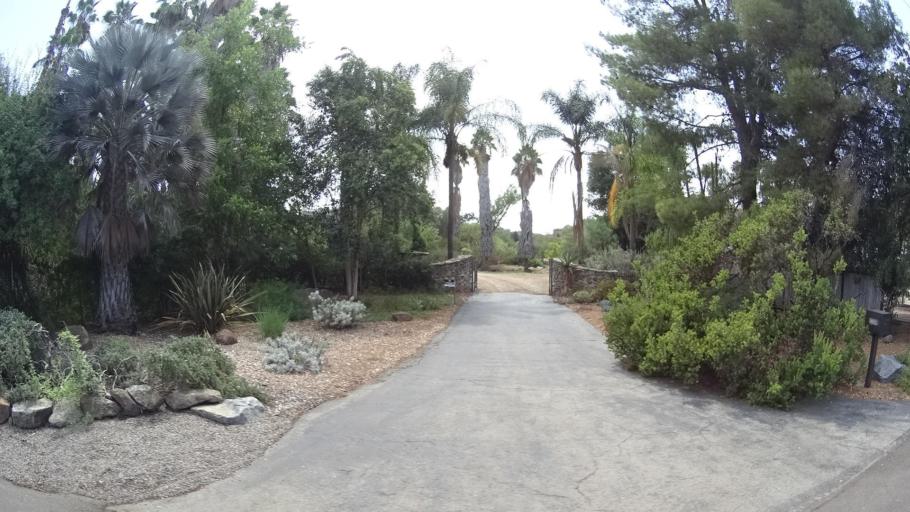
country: US
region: California
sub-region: San Diego County
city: Escondido
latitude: 33.1092
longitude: -117.0379
